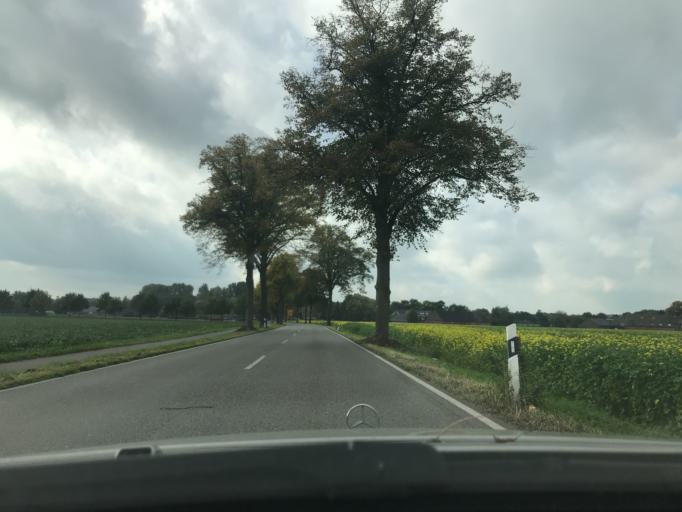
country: DE
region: North Rhine-Westphalia
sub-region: Regierungsbezirk Dusseldorf
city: Krefeld
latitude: 51.4133
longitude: 6.5653
